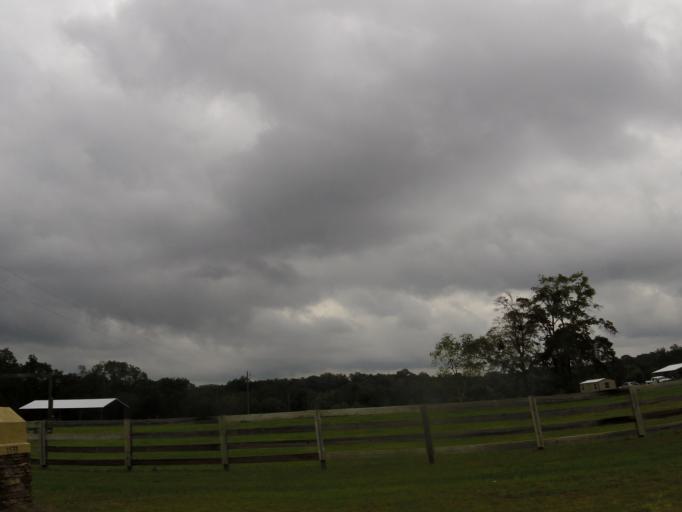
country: US
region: Florida
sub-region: Clay County
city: Middleburg
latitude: 30.1160
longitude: -81.9491
